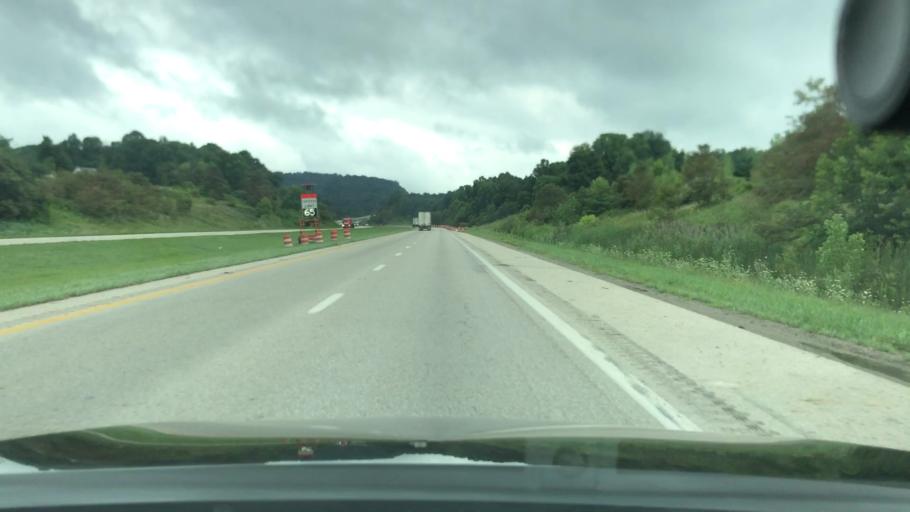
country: US
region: Ohio
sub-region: Ross County
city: Chillicothe
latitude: 39.2480
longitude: -82.8479
